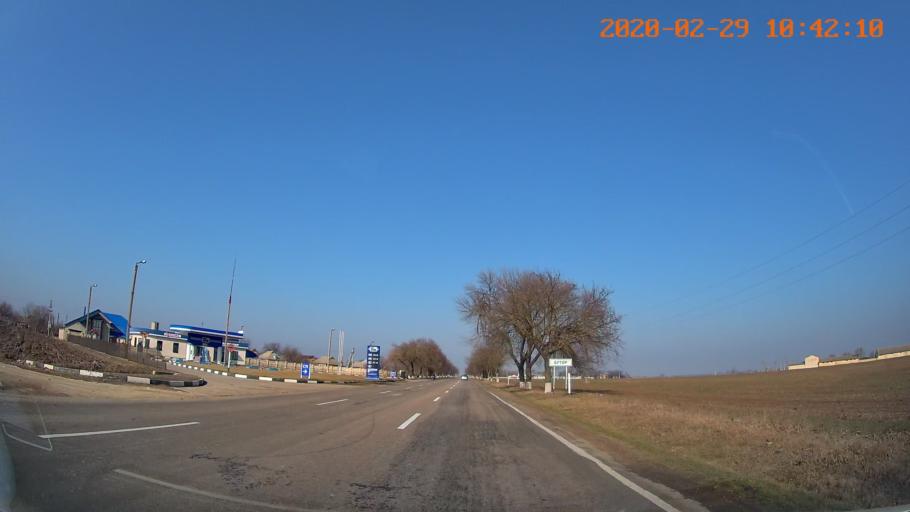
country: MD
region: Telenesti
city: Grigoriopol
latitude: 47.0493
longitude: 29.4146
